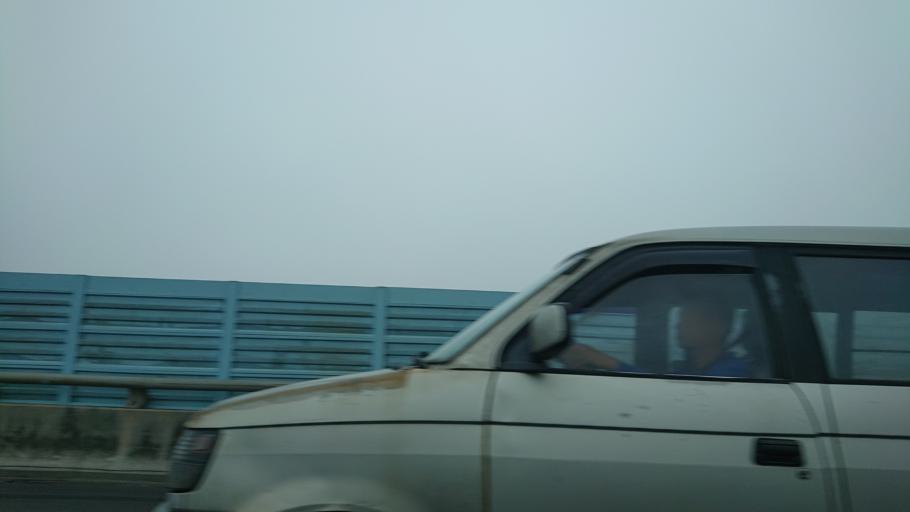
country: TW
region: Taiwan
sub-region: Hsinchu
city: Hsinchu
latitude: 24.7061
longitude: 120.8784
